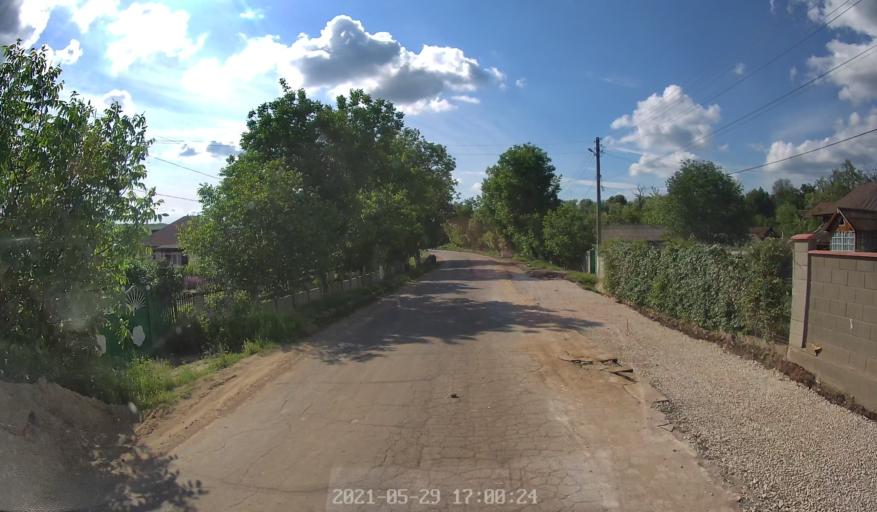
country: MD
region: Chisinau
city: Singera
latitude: 46.8289
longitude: 28.8661
